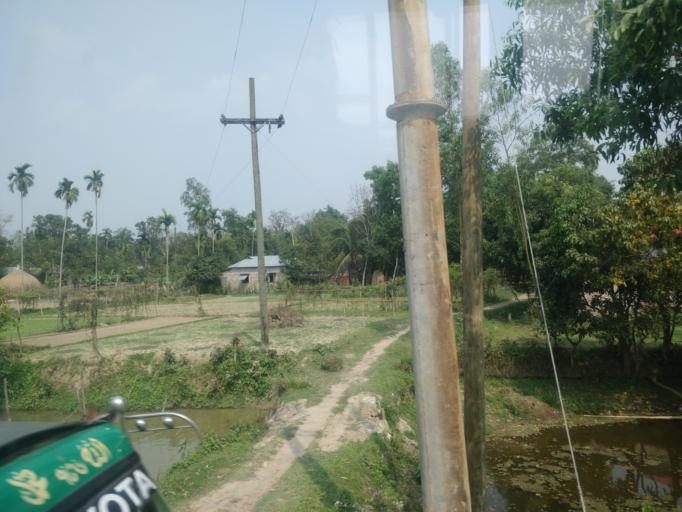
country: BD
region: Sylhet
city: Habiganj
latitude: 24.3265
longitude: 91.4326
